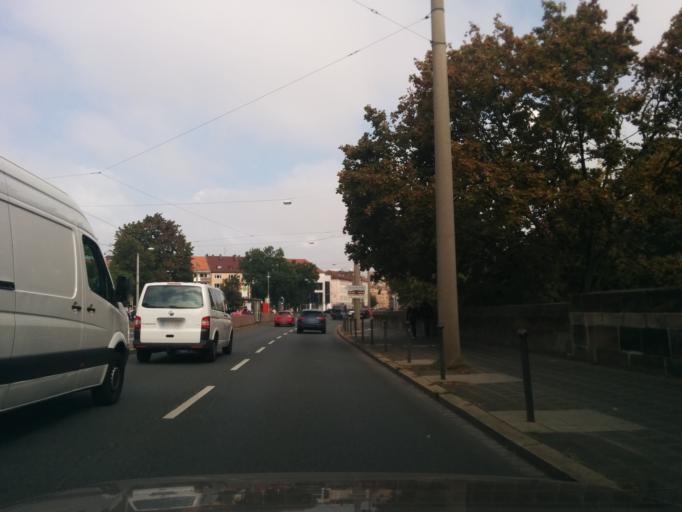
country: DE
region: Bavaria
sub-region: Regierungsbezirk Mittelfranken
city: Nuernberg
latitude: 49.4504
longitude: 11.0663
